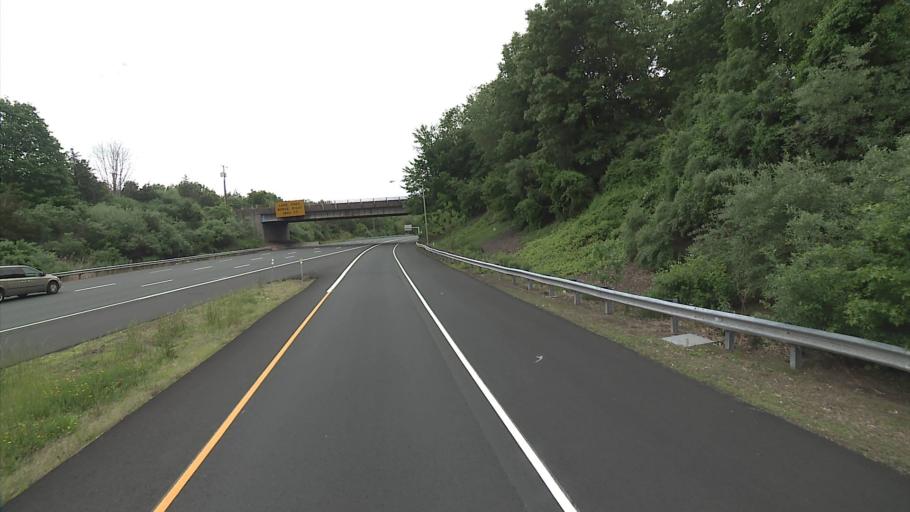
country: US
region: Connecticut
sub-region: Middlesex County
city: Cromwell
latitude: 41.6210
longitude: -72.6850
